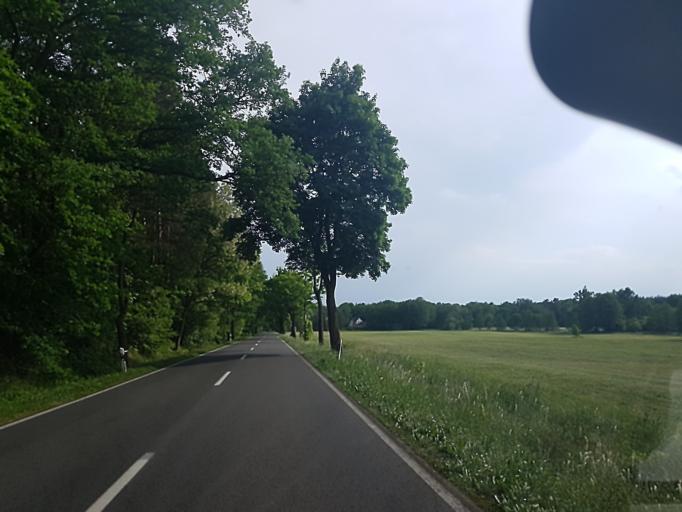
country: DE
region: Saxony-Anhalt
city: Nudersdorf
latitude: 51.9473
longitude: 12.6009
